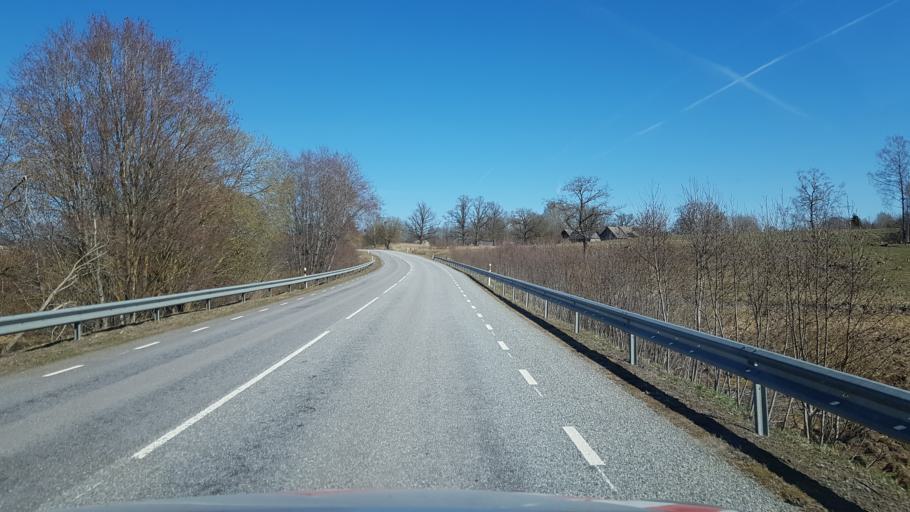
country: EE
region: Laeaene-Virumaa
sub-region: Vinni vald
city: Vinni
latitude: 59.3178
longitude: 26.4837
